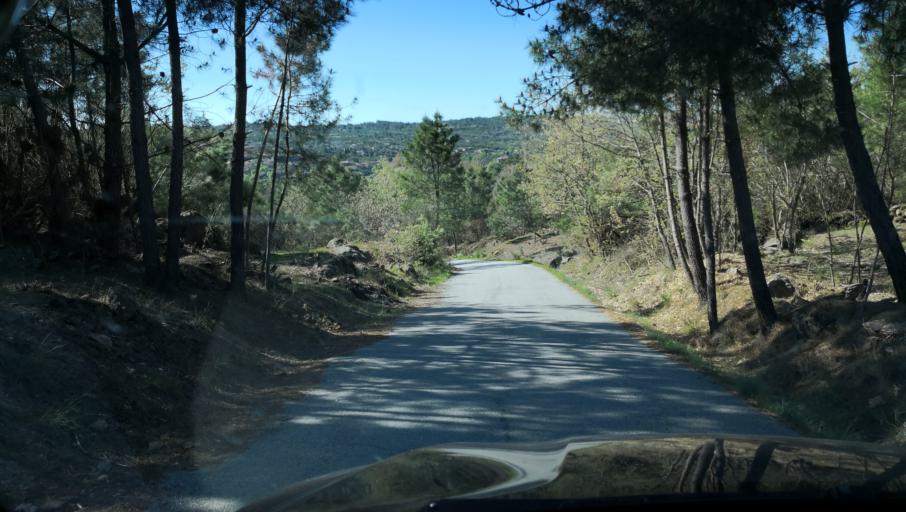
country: PT
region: Vila Real
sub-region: Sabrosa
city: Sabrosa
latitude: 41.2964
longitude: -7.6380
